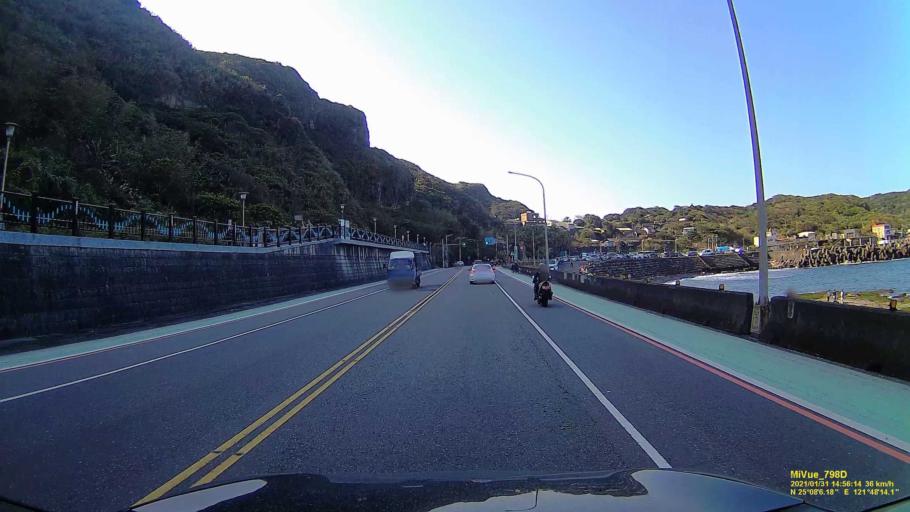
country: TW
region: Taiwan
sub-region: Keelung
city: Keelung
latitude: 25.1351
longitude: 121.8036
